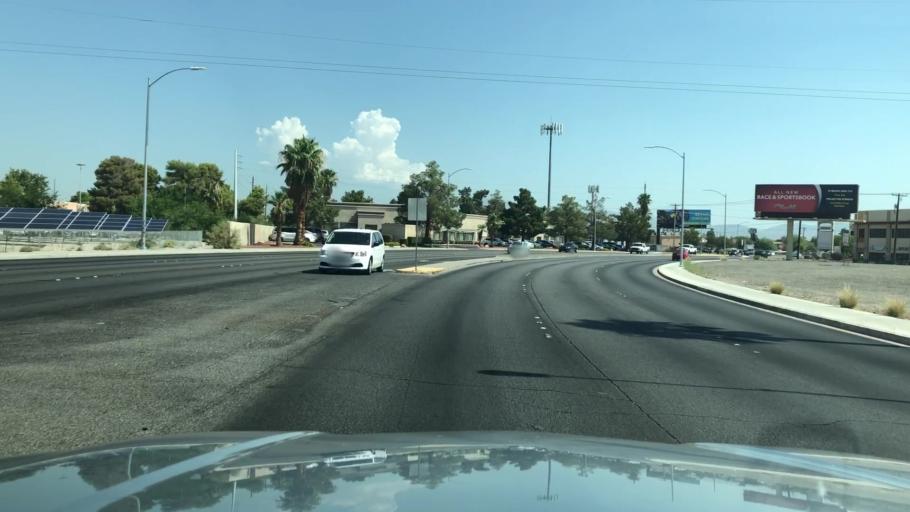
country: US
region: Nevada
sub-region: Clark County
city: Spring Valley
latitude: 36.1556
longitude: -115.2257
